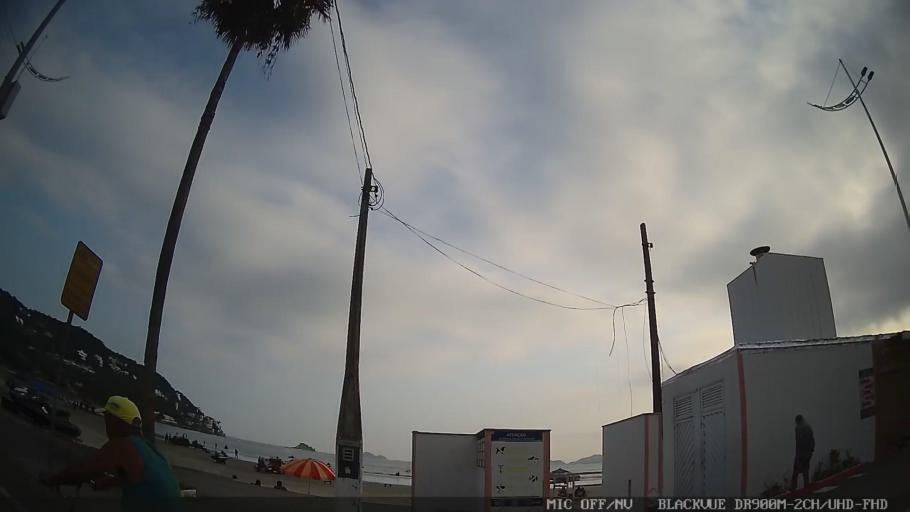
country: BR
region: Sao Paulo
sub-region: Guaruja
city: Guaruja
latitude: -23.9900
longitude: -46.2029
